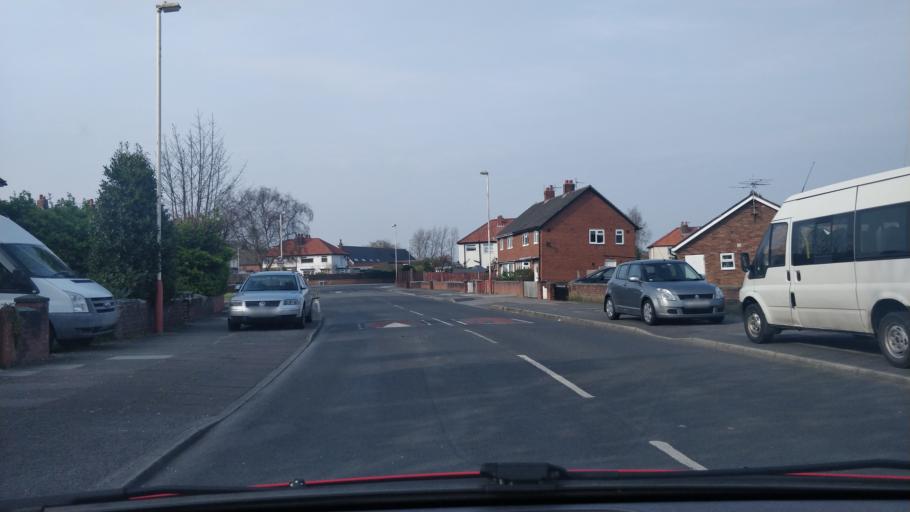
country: GB
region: England
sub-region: Sefton
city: Formby
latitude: 53.5972
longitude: -3.0333
